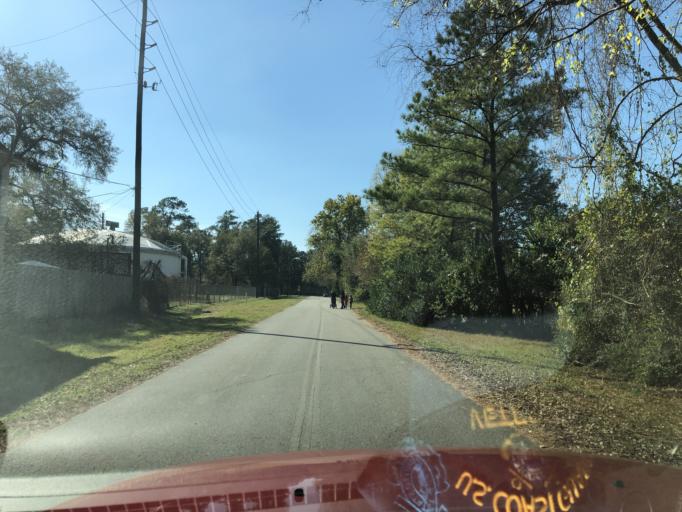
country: US
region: Texas
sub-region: Harris County
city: Tomball
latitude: 30.0296
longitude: -95.5415
